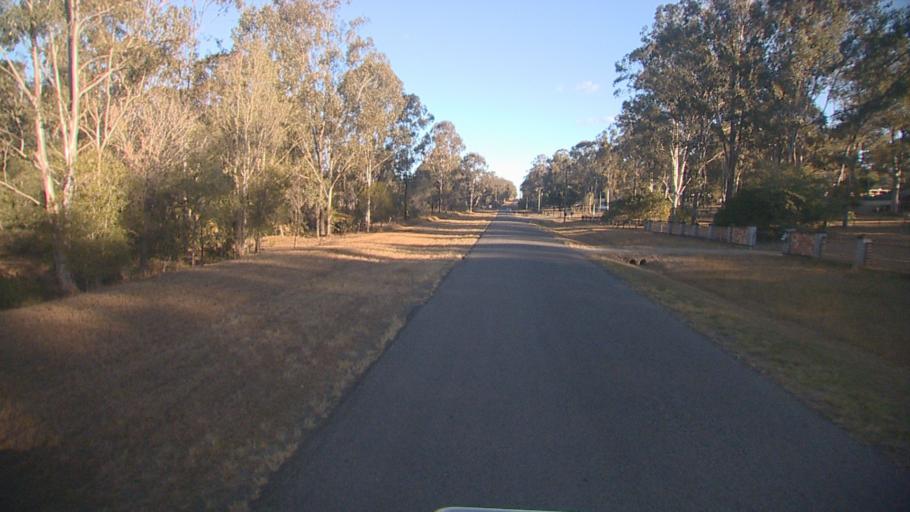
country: AU
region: Queensland
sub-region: Logan
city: Cedar Vale
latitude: -27.8625
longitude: 152.9778
